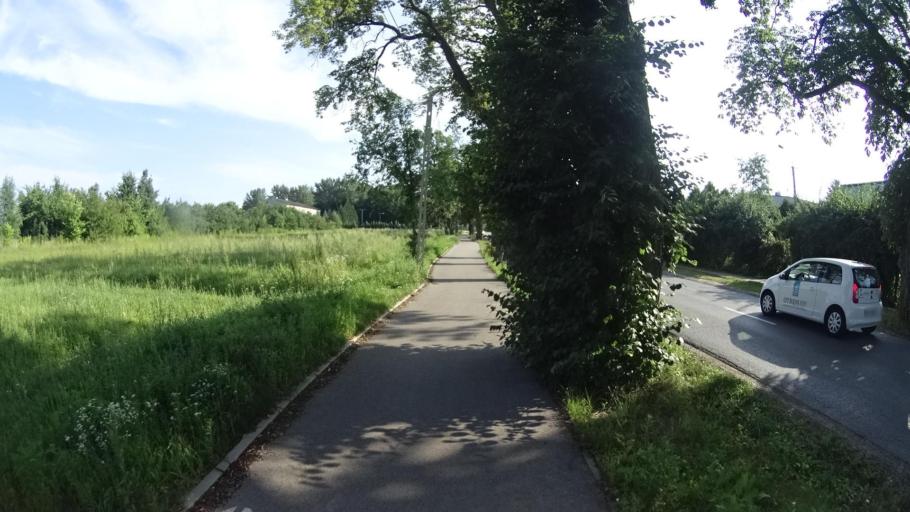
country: PL
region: Masovian Voivodeship
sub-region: Powiat pruszkowski
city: Nadarzyn
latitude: 52.0518
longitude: 20.7836
